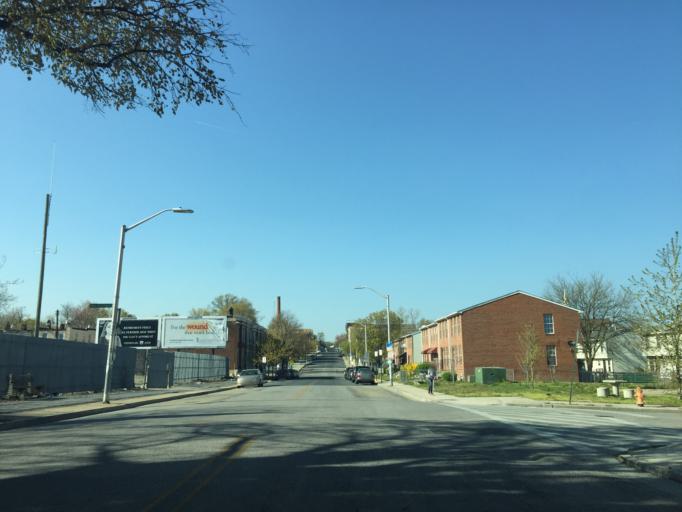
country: US
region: Maryland
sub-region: City of Baltimore
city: Baltimore
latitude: 39.3021
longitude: -76.6431
